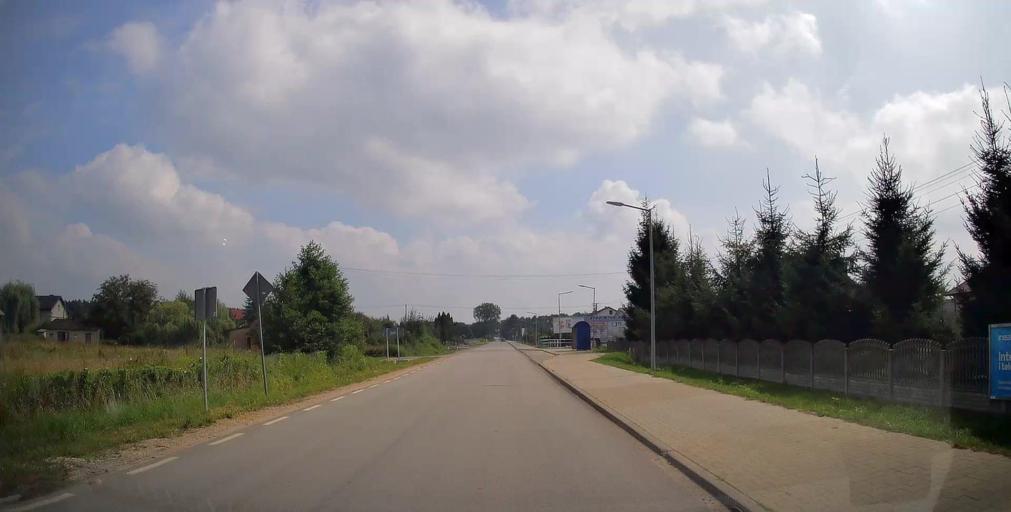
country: PL
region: Masovian Voivodeship
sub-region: Powiat bialobrzeski
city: Sucha
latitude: 51.6169
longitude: 20.9576
